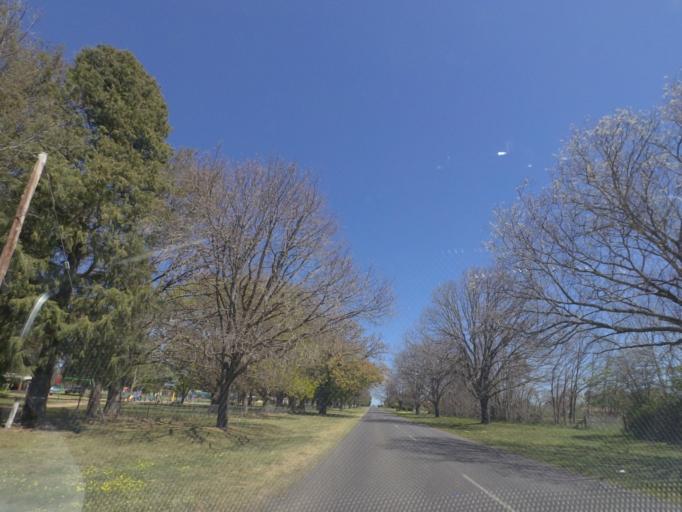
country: AU
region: Victoria
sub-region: Hume
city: Sunbury
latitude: -37.2792
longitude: 144.7266
